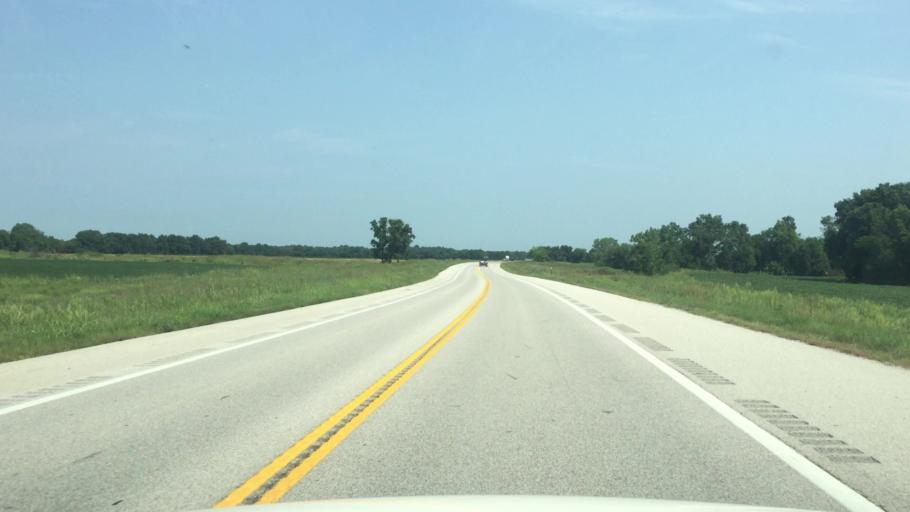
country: US
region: Kansas
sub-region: Montgomery County
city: Coffeyville
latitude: 37.1162
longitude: -95.5835
